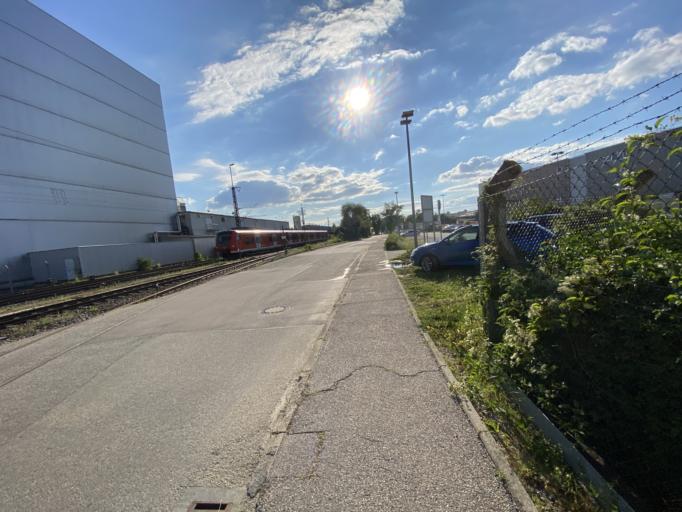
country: DE
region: Bavaria
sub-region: Lower Bavaria
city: Dingolfing
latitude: 48.6414
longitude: 12.4789
